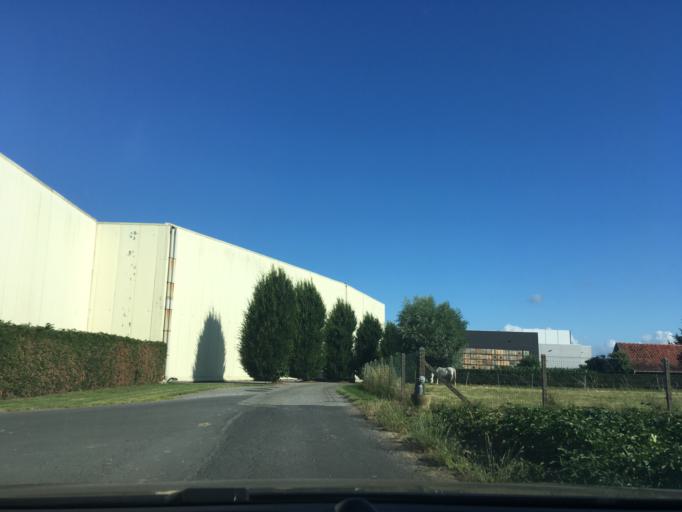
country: BE
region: Flanders
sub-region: Provincie West-Vlaanderen
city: Ardooie
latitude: 50.9697
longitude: 3.2031
